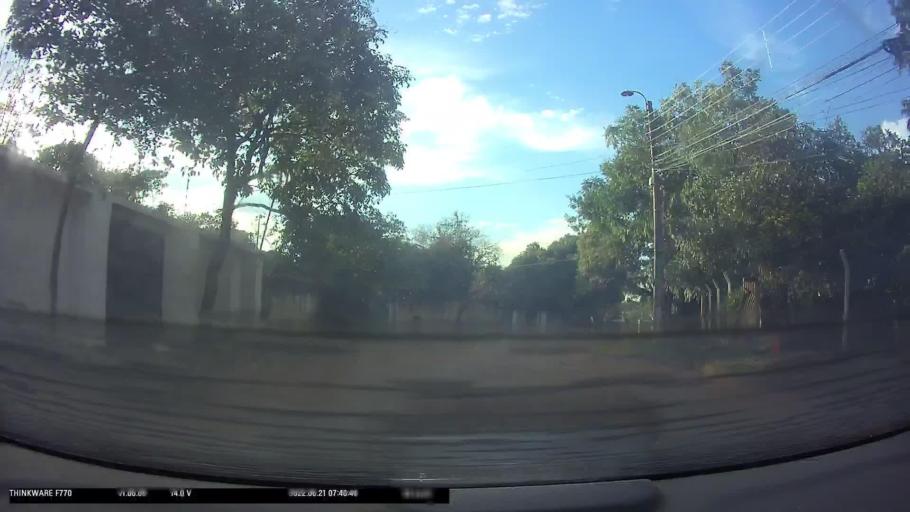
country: PY
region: Central
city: Limpio
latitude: -25.2458
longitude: -57.5077
